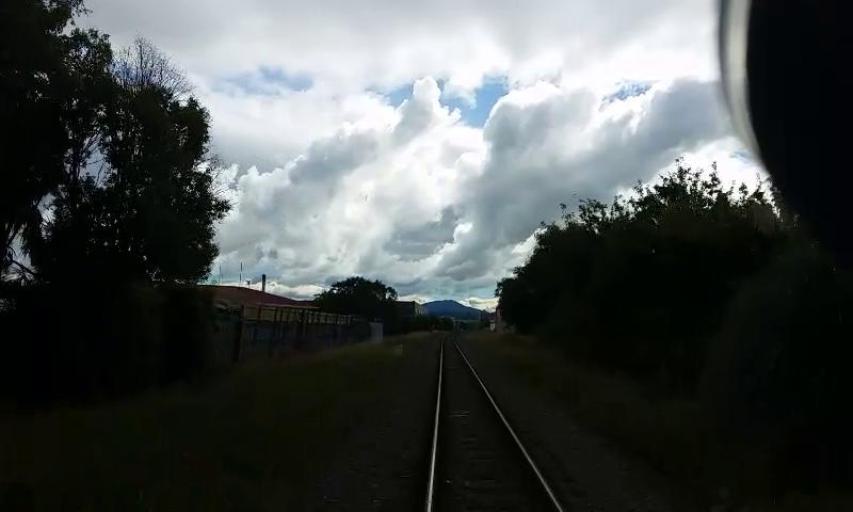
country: NZ
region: Canterbury
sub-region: Waimakariri District
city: Woodend
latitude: -43.3059
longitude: 172.5990
